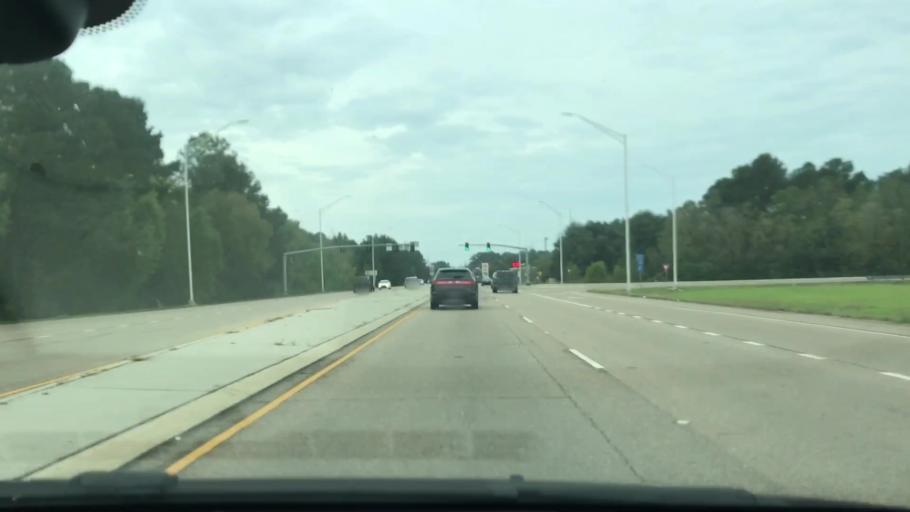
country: US
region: Louisiana
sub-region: Saint Tammany Parish
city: Slidell
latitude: 30.3092
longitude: -89.7712
